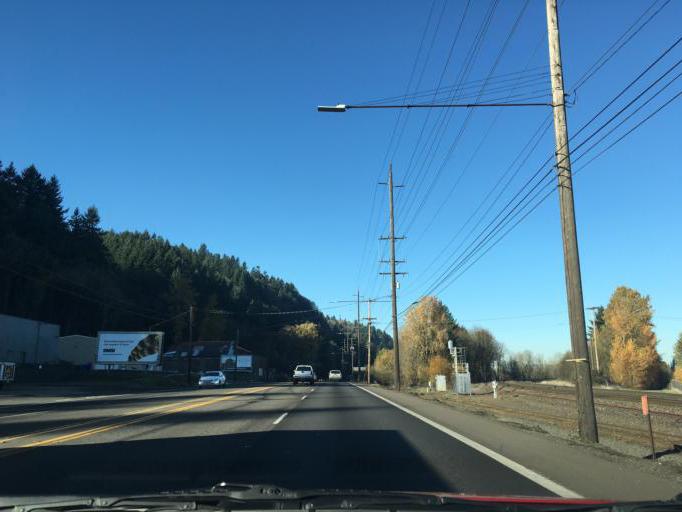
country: US
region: Oregon
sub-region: Washington County
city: West Haven
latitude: 45.5669
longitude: -122.7504
